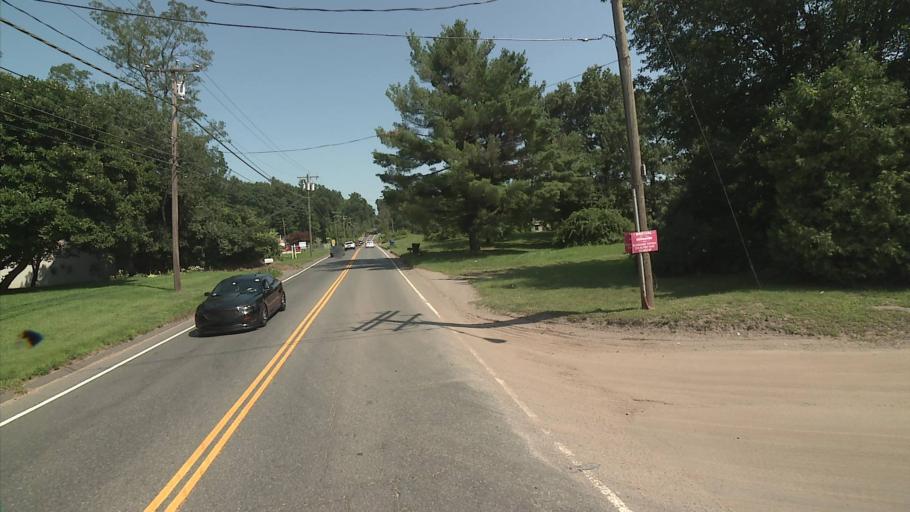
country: US
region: Connecticut
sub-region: Hartford County
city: Blue Hills
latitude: 41.8610
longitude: -72.6930
